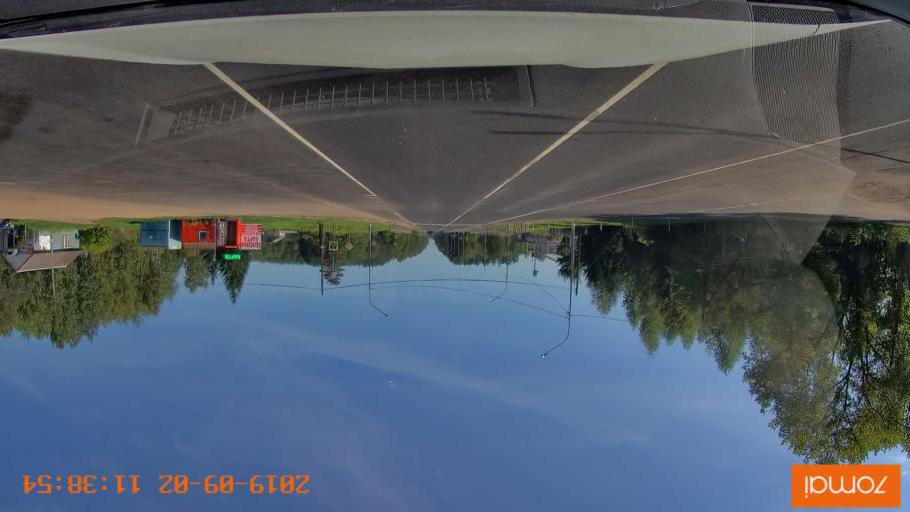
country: RU
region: Smolensk
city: Oster
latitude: 53.9109
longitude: 32.7327
